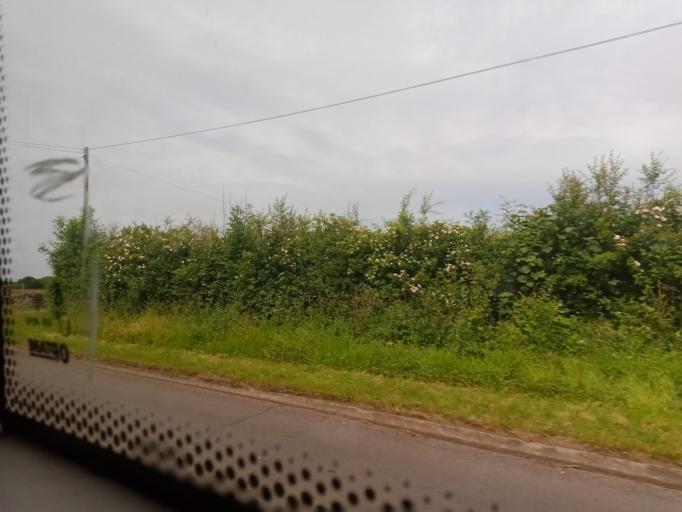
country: GB
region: Wales
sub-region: Anglesey
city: Llanfairpwllgwyngyll
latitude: 53.2280
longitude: -4.1875
